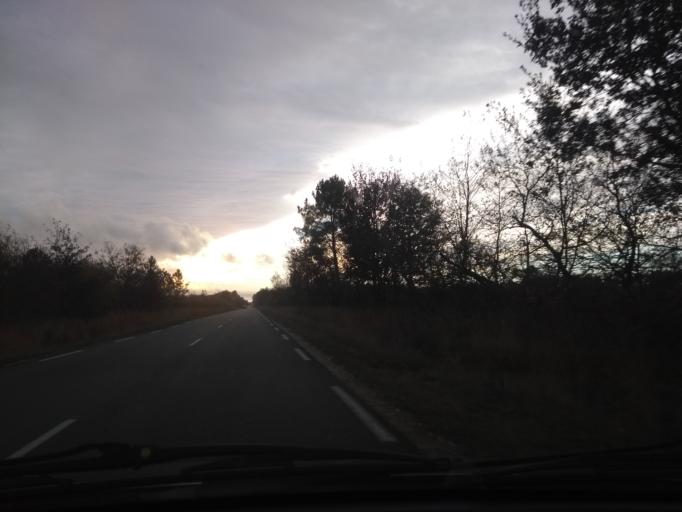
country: FR
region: Aquitaine
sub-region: Departement de la Gironde
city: Le Barp
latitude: 44.6121
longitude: -0.6857
